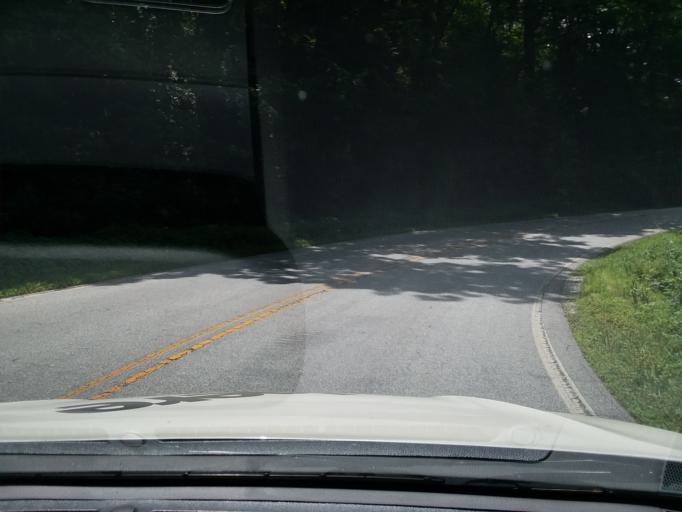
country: US
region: Georgia
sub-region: Rabun County
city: Mountain City
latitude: 35.0288
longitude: -83.1858
